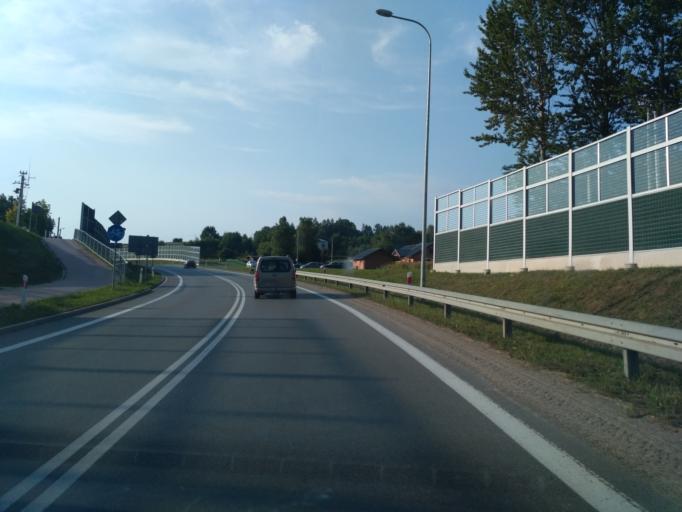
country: PL
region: Subcarpathian Voivodeship
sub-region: Powiat brzozowski
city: Humniska
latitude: 49.6865
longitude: 22.0384
